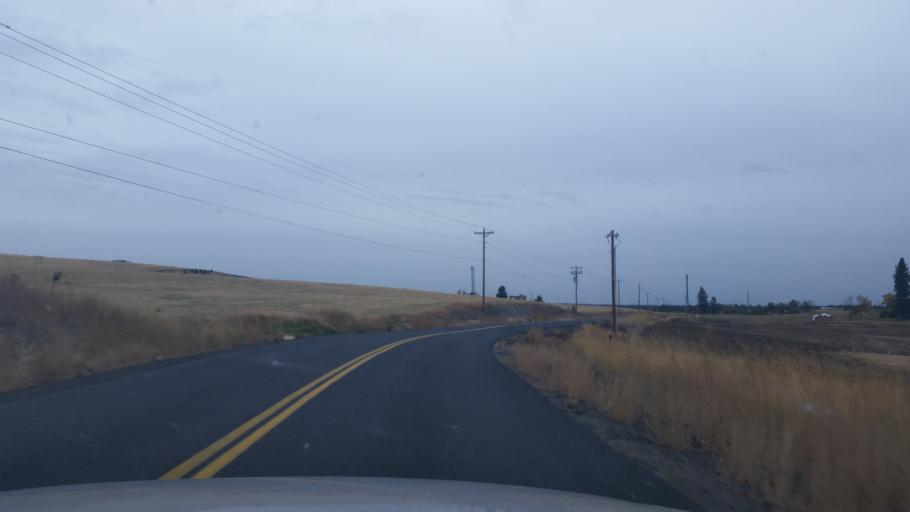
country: US
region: Washington
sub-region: Spokane County
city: Cheney
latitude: 47.5319
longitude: -117.5507
